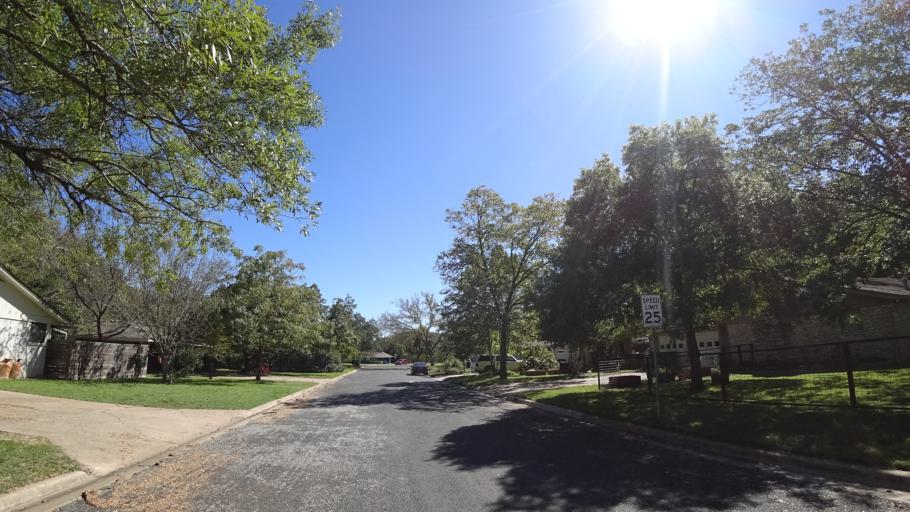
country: US
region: Texas
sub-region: Travis County
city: Rollingwood
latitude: 30.2286
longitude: -97.7981
